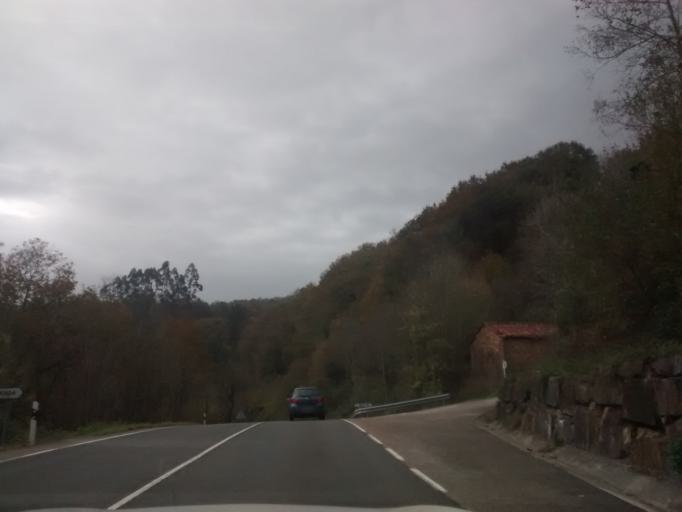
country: ES
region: Cantabria
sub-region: Provincia de Cantabria
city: Santiurde de Toranzo
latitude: 43.1658
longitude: -3.8973
